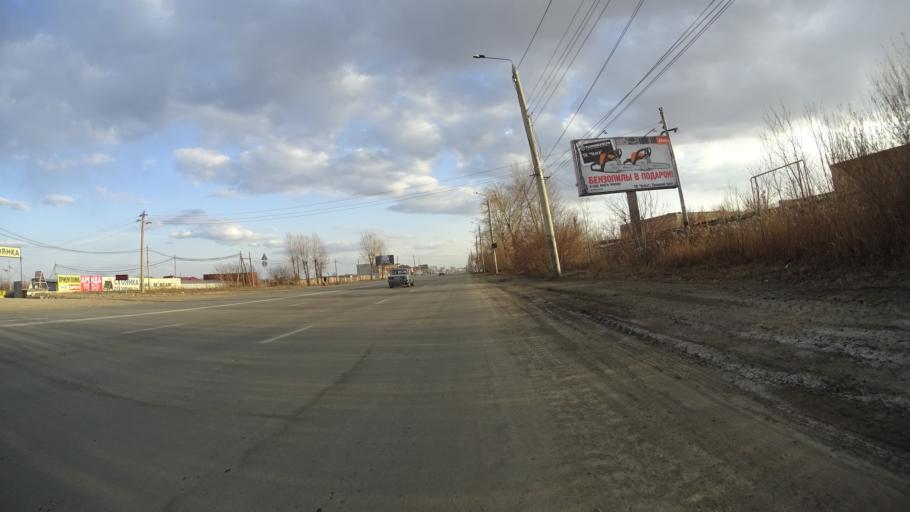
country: RU
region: Chelyabinsk
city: Novosineglazovskiy
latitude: 55.0970
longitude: 61.3877
